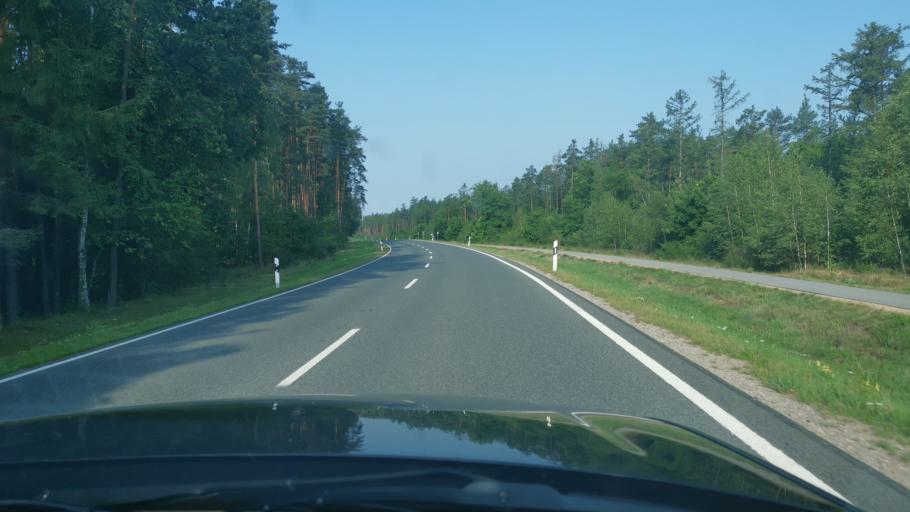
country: DE
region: Bavaria
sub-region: Upper Palatinate
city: Wernberg-Koblitz
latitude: 49.5405
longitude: 12.1093
